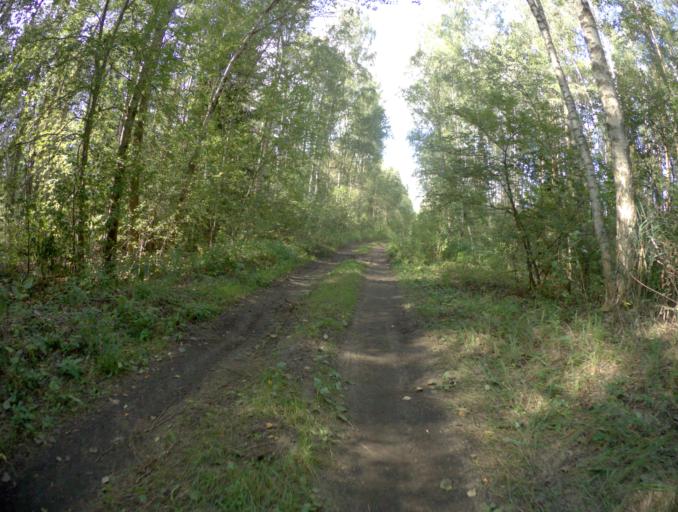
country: RU
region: Vladimir
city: Sobinka
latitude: 55.9414
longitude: 40.0586
